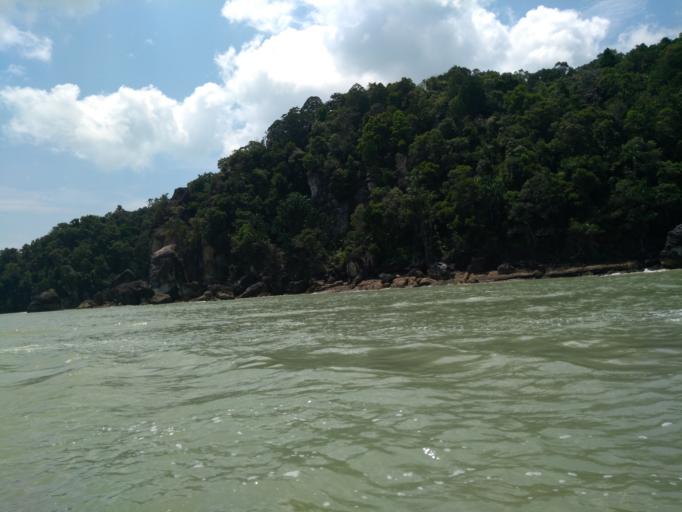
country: MY
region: Sarawak
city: Kuching
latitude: 1.7262
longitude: 110.4425
